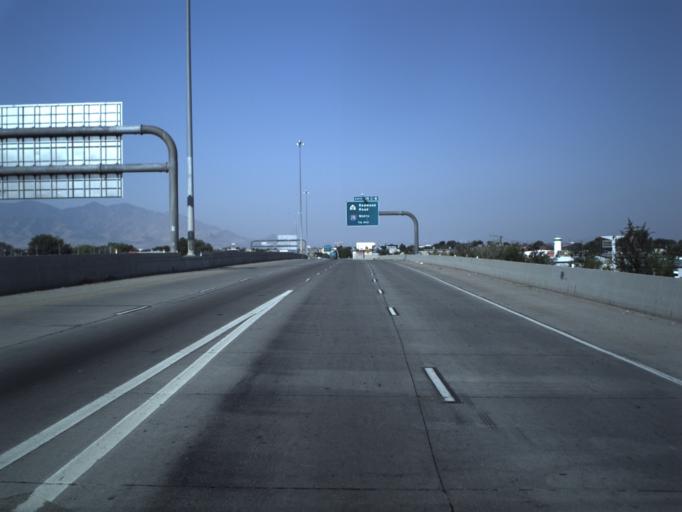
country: US
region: Utah
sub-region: Salt Lake County
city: South Salt Lake
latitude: 40.7243
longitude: -111.9178
